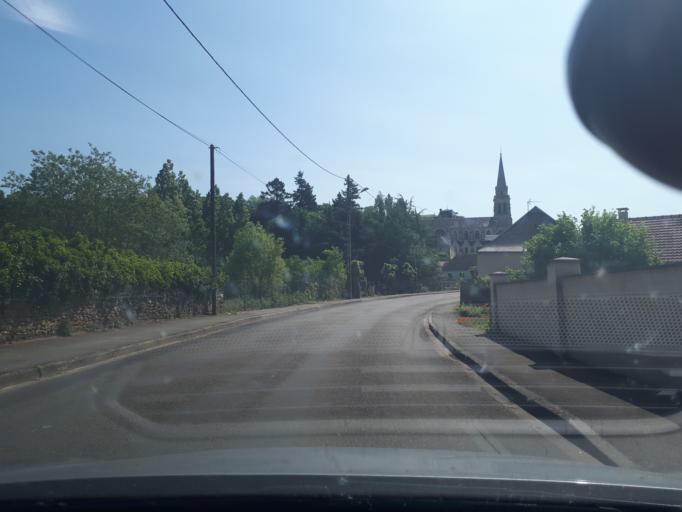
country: FR
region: Pays de la Loire
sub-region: Departement de la Sarthe
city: Montfort-le-Gesnois
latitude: 48.0503
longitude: 0.4009
